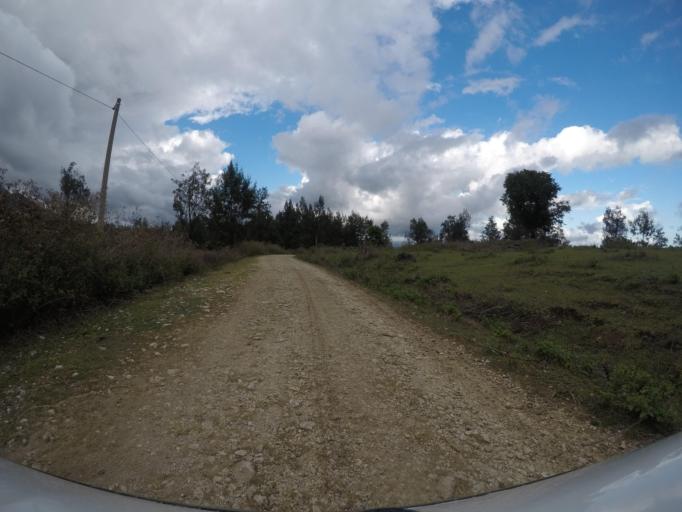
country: TL
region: Baucau
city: Venilale
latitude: -8.6805
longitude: 126.6401
